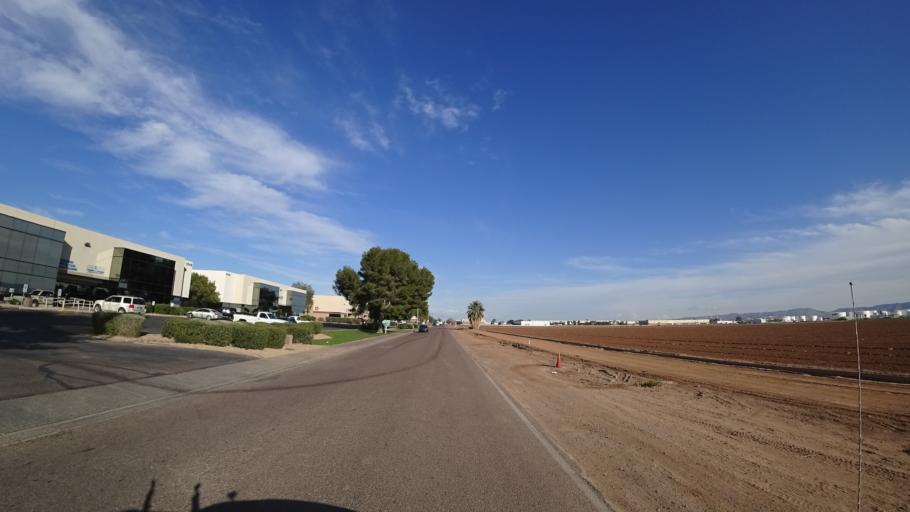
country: US
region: Arizona
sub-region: Maricopa County
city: Tolleson
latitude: 33.4587
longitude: -112.1806
